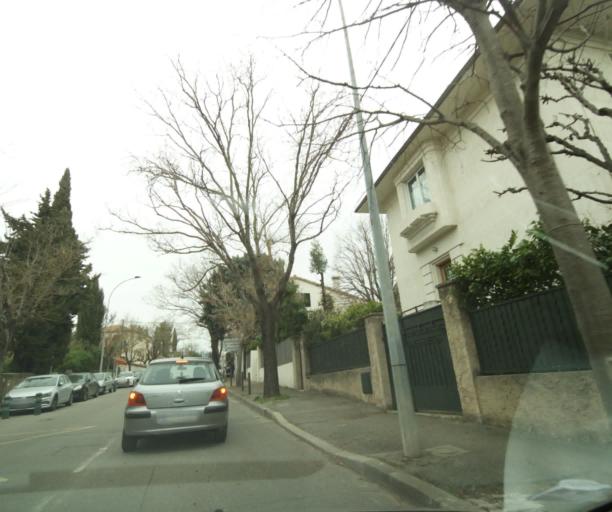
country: FR
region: Provence-Alpes-Cote d'Azur
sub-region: Departement des Bouches-du-Rhone
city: Aix-en-Provence
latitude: 43.5197
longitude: 5.4565
